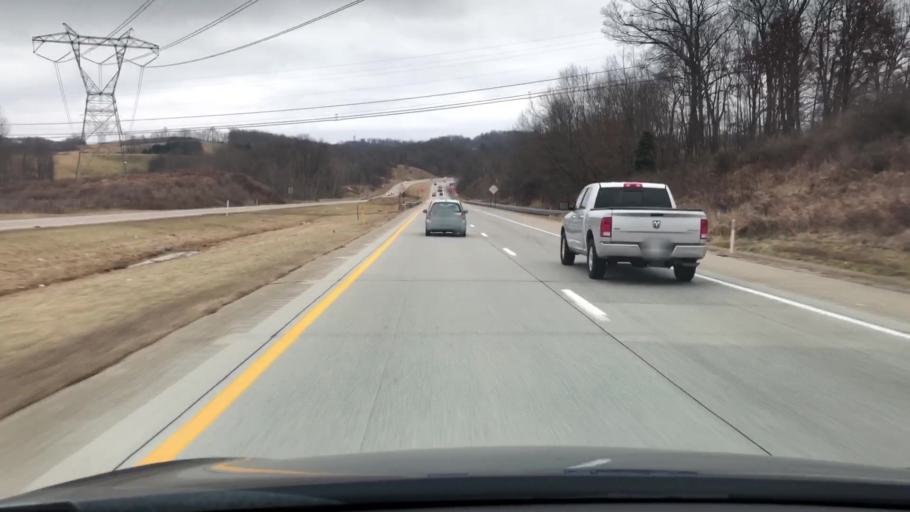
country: US
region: West Virginia
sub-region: Monongalia County
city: Star City
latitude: 39.7440
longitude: -80.0657
